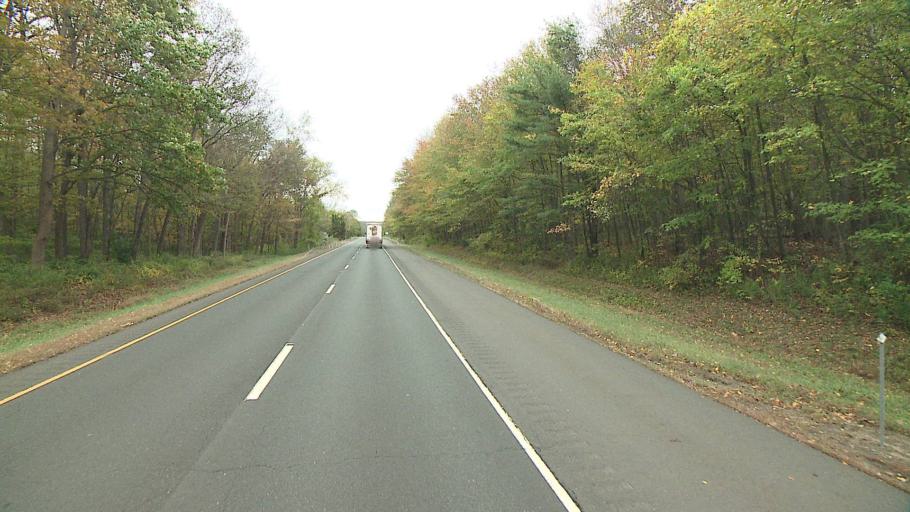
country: US
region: Connecticut
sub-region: Middlesex County
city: Higganum
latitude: 41.5016
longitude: -72.5798
